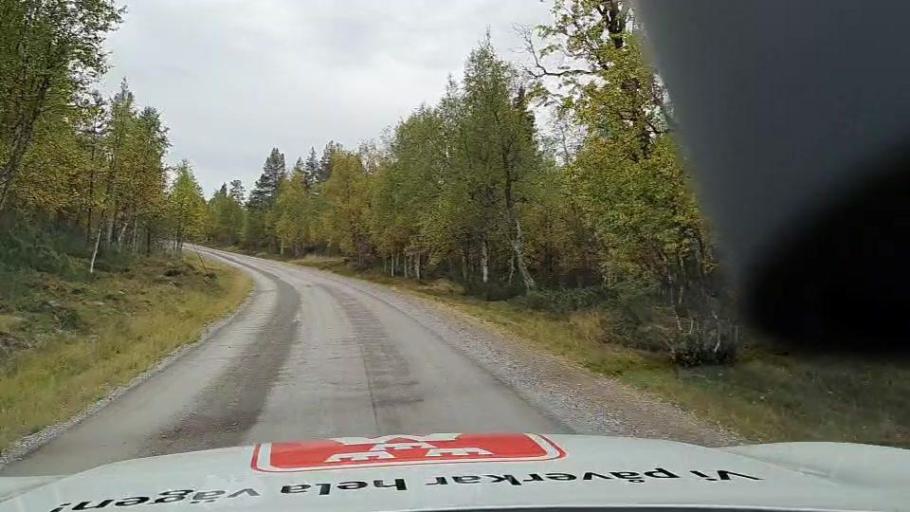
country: NO
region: Hedmark
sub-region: Engerdal
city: Engerdal
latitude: 62.0779
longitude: 12.7441
